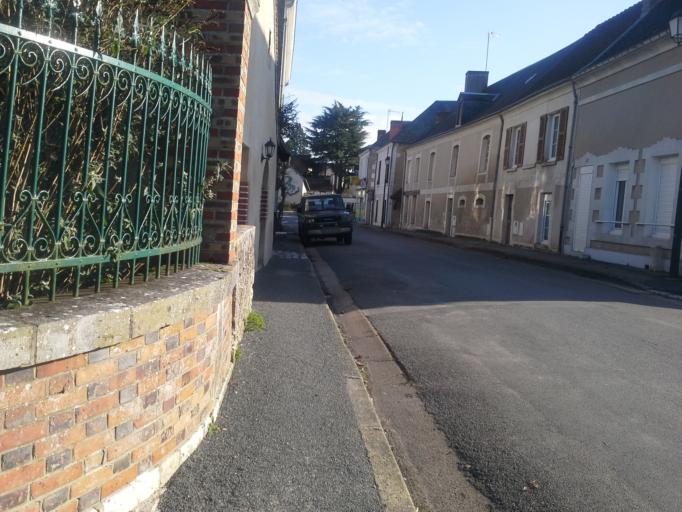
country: FR
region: Centre
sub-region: Departement du Loir-et-Cher
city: Villiers-sur-Loir
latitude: 47.8065
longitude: 0.9937
